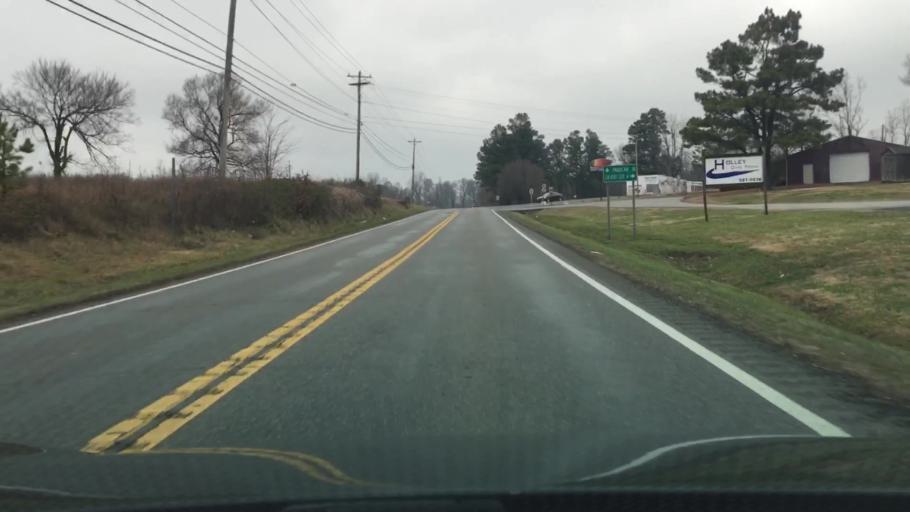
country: US
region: Kentucky
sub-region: Marshall County
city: Calvert City
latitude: 36.9460
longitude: -88.3650
